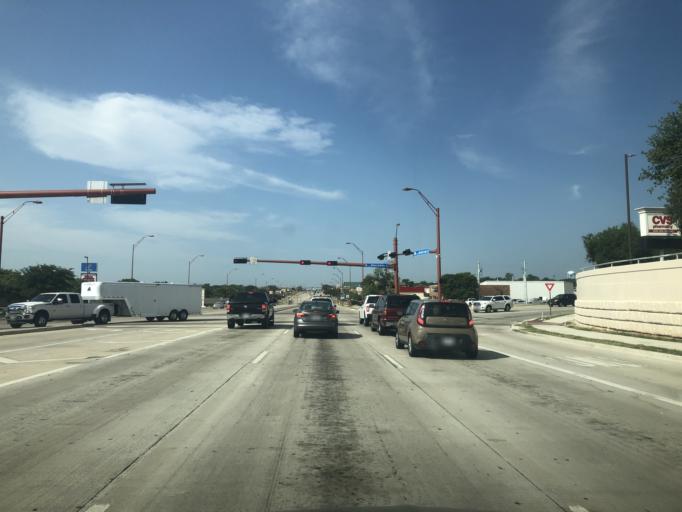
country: US
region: Texas
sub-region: Tarrant County
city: Benbrook
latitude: 32.6795
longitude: -97.4639
